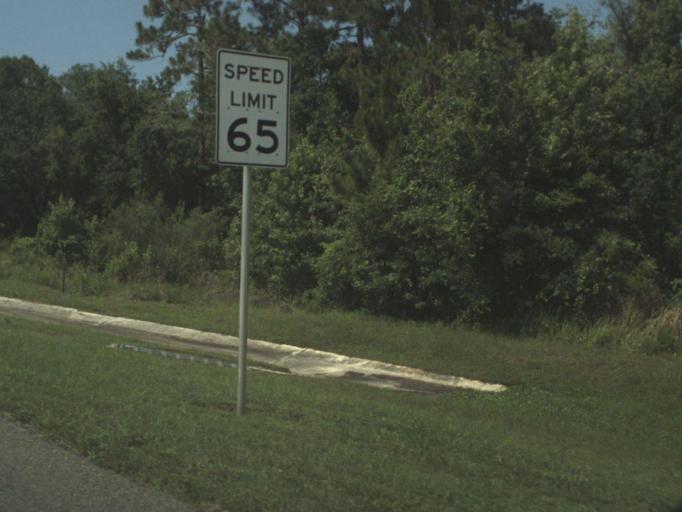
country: US
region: Florida
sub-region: Orange County
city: Christmas
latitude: 28.3956
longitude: -80.9444
